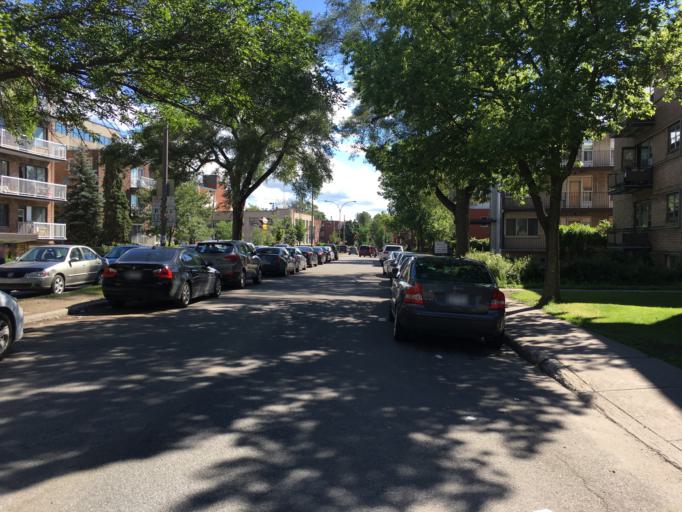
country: CA
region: Quebec
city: Mont-Royal
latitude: 45.5014
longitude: -73.6304
